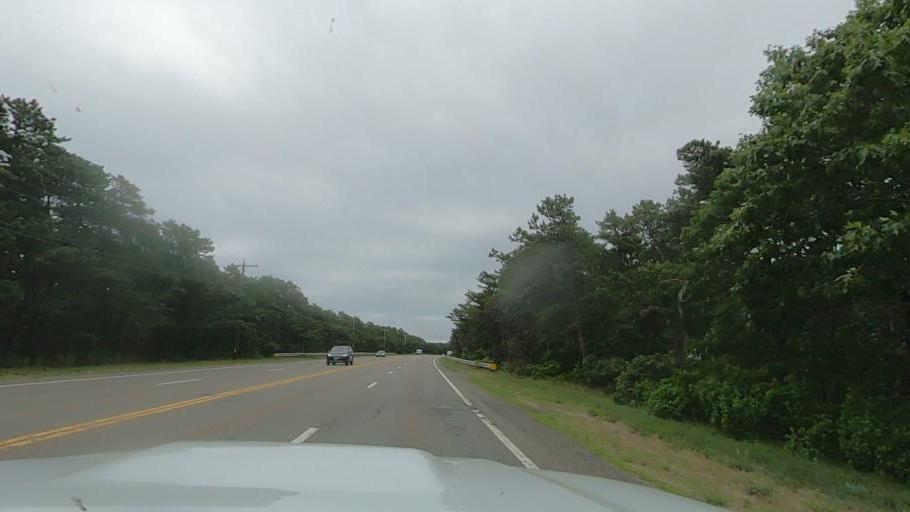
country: US
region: Massachusetts
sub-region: Barnstable County
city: Truro
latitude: 42.0471
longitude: -70.1013
